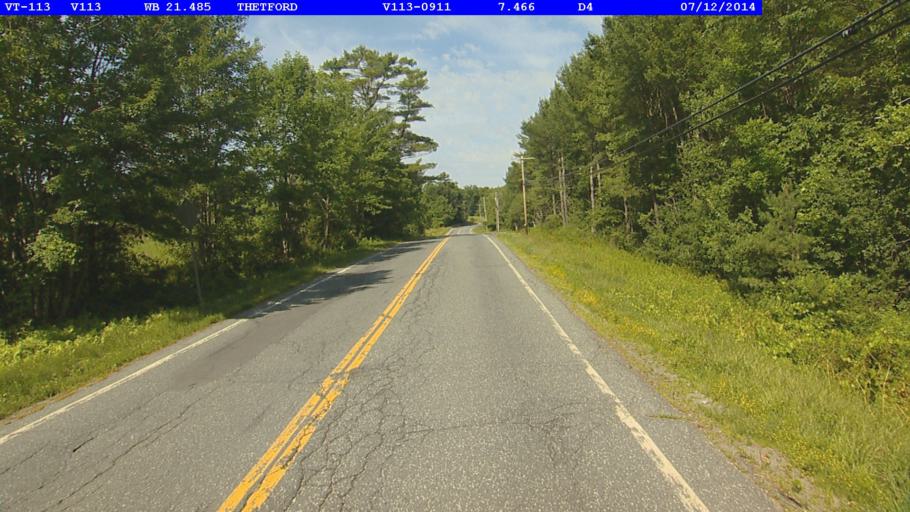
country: US
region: New Hampshire
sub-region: Grafton County
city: Lyme
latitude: 43.8121
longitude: -72.2081
